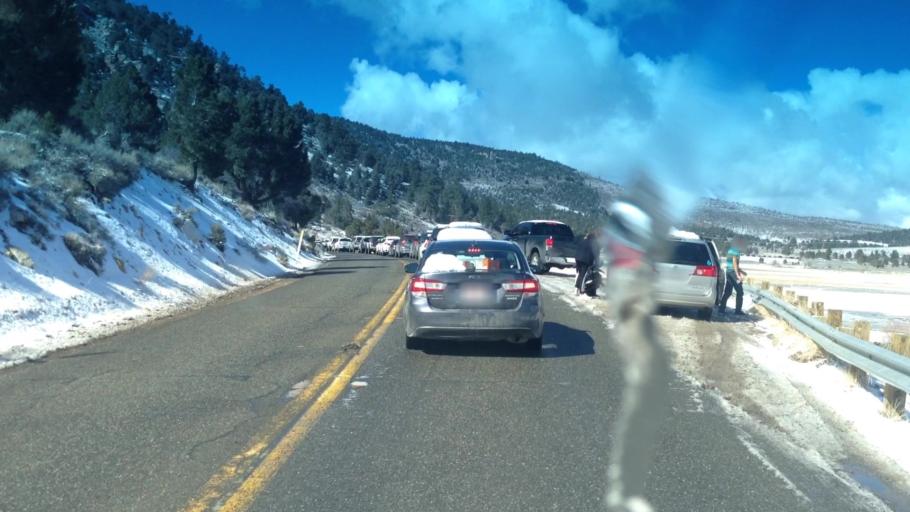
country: US
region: California
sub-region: San Bernardino County
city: Big Bear City
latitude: 34.2822
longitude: -116.8162
